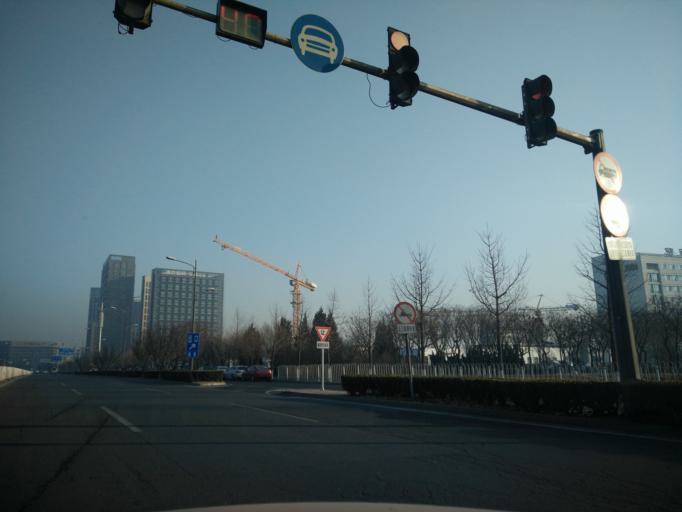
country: CN
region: Beijing
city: Jiugong
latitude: 39.7731
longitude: 116.5113
